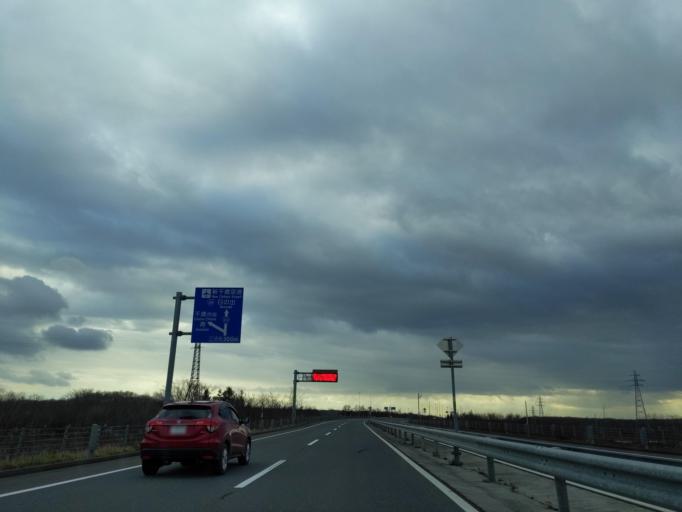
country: JP
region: Hokkaido
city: Chitose
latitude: 42.8302
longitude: 141.6902
